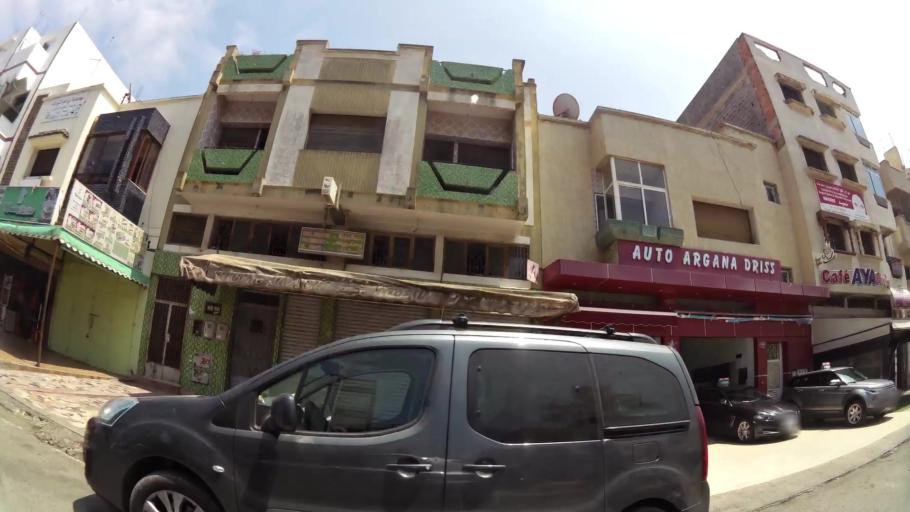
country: MA
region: Rabat-Sale-Zemmour-Zaer
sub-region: Skhirate-Temara
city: Temara
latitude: 33.9771
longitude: -6.8901
